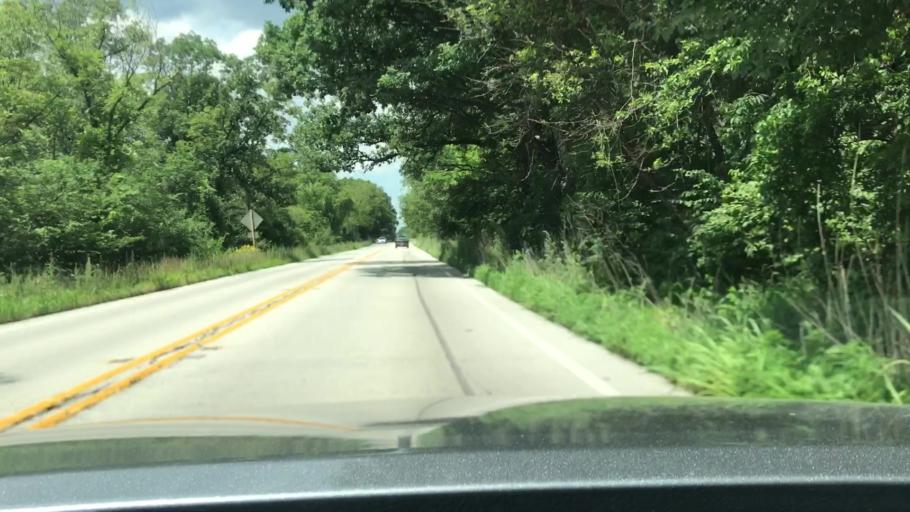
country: US
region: Illinois
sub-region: Cook County
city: Willow Springs
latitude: 41.7175
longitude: -87.8687
